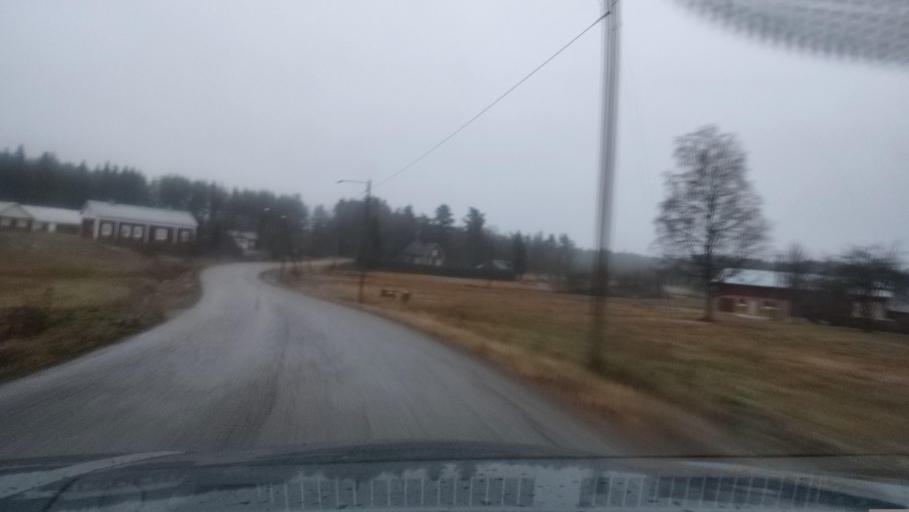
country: FI
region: Southern Ostrobothnia
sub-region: Suupohja
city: Karijoki
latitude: 62.1299
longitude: 21.5789
